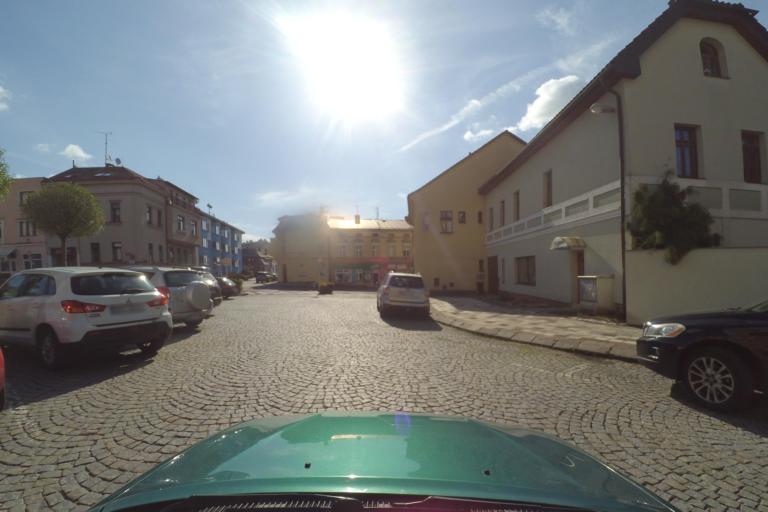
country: CZ
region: Kralovehradecky
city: Dvur Kralove nad Labem
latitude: 50.4300
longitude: 15.8128
